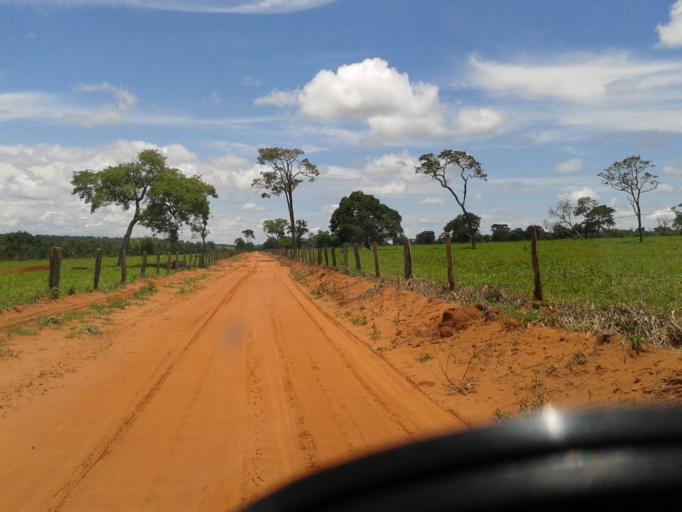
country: BR
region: Minas Gerais
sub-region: Santa Vitoria
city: Santa Vitoria
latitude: -18.9437
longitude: -49.8613
